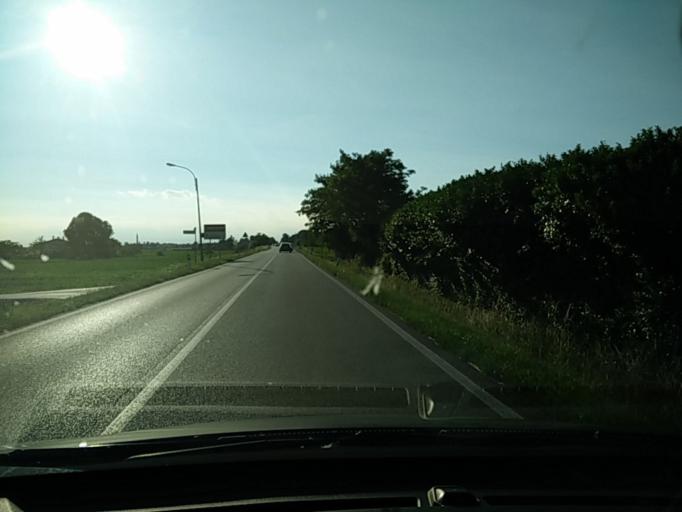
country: IT
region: Veneto
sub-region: Provincia di Venezia
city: Passarella
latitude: 45.5907
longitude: 12.6282
